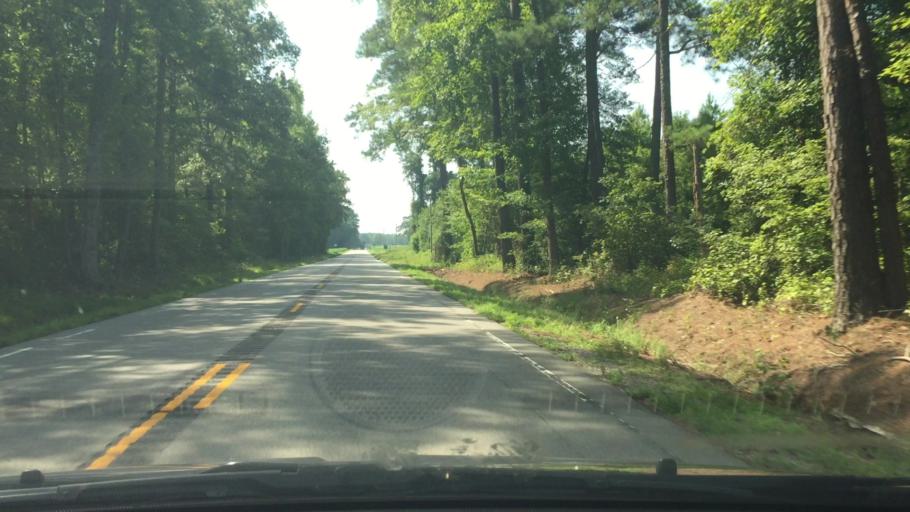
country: US
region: Virginia
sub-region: Southampton County
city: Courtland
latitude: 36.8544
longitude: -77.1349
